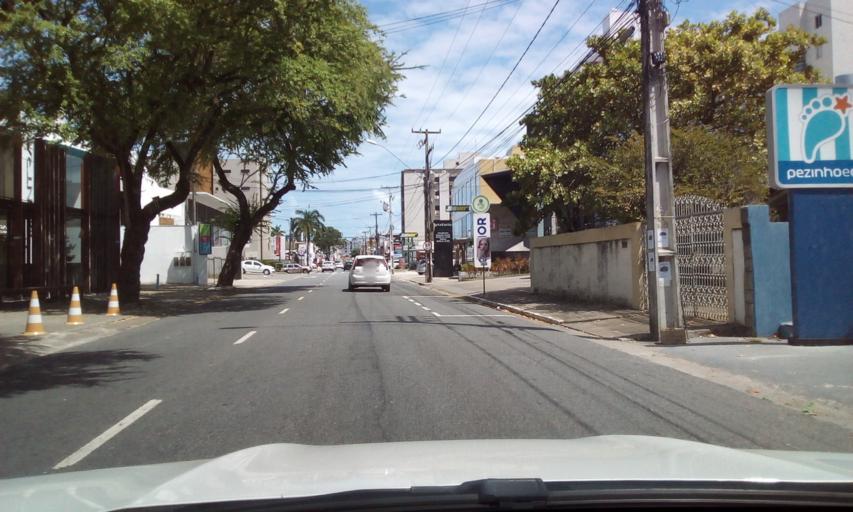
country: BR
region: Paraiba
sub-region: Joao Pessoa
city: Joao Pessoa
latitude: -7.1047
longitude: -34.8312
